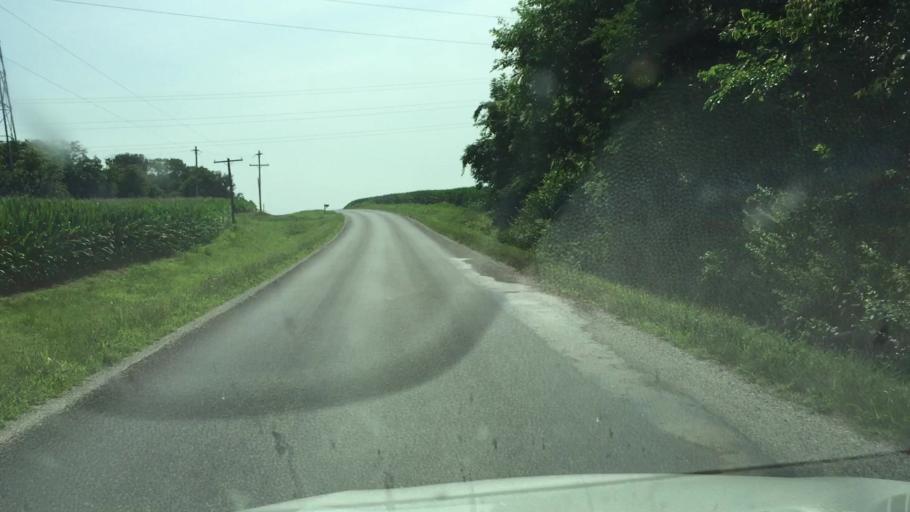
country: US
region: Illinois
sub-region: Hancock County
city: Nauvoo
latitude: 40.5117
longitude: -91.3525
